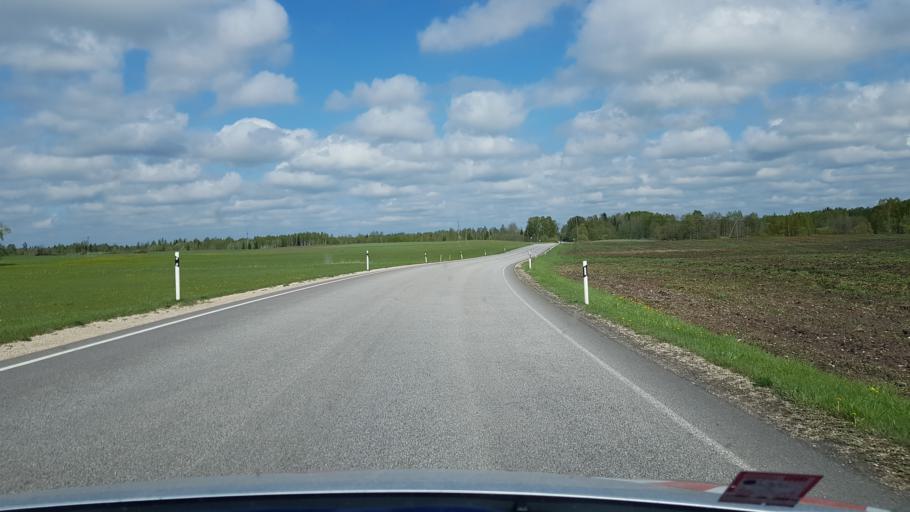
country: EE
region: Valgamaa
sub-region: Torva linn
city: Torva
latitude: 58.0167
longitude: 25.7992
